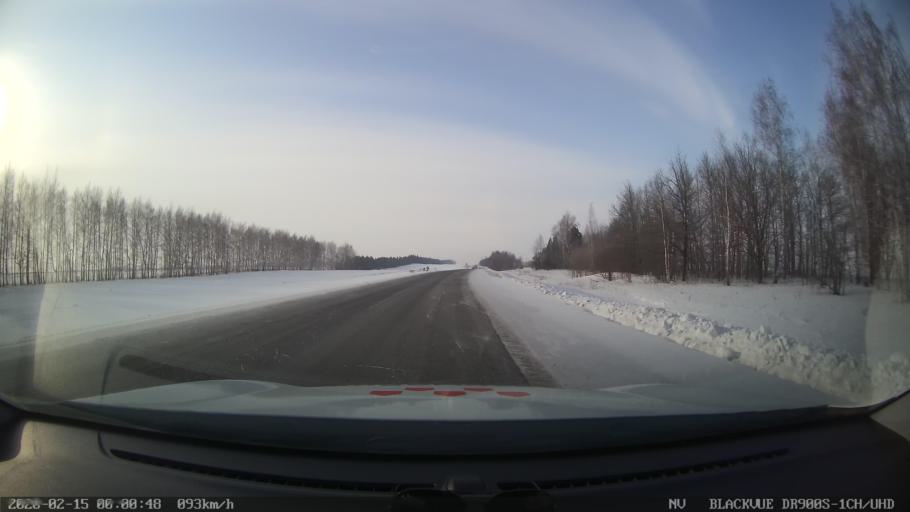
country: RU
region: Tatarstan
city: Kuybyshevskiy Zaton
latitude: 55.3441
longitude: 49.0304
